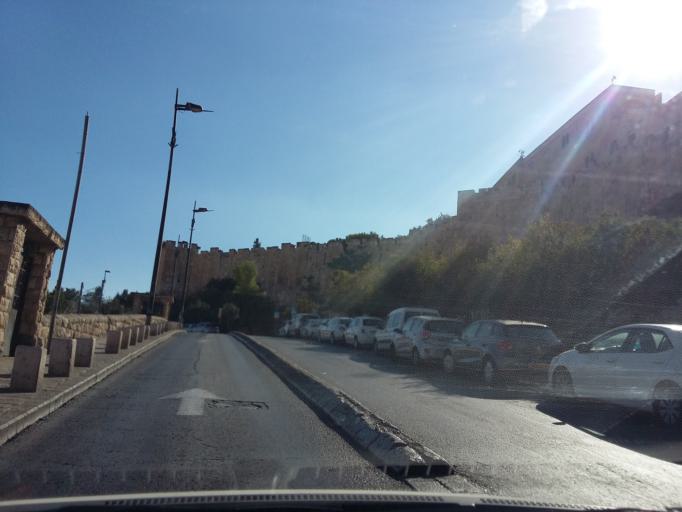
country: PS
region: West Bank
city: Old City
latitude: 31.7742
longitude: 35.2335
